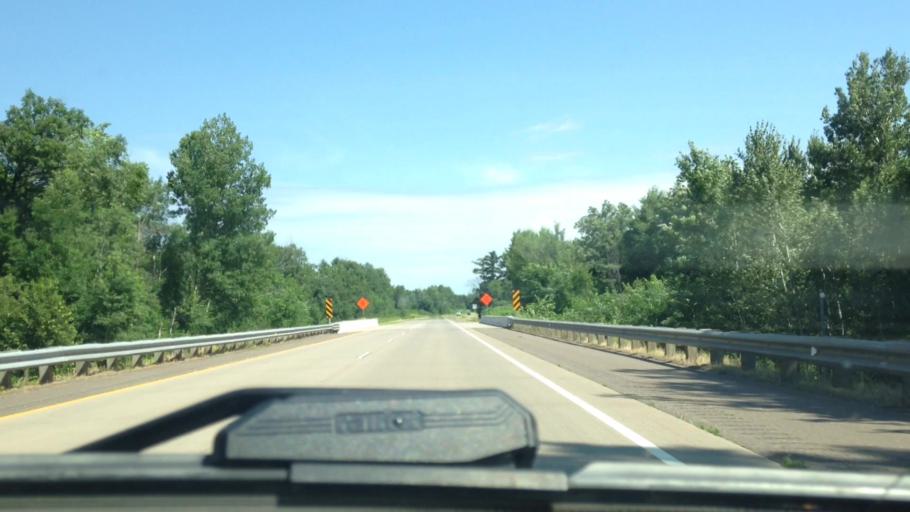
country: US
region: Wisconsin
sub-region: Barron County
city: Rice Lake
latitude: 45.5530
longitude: -91.7645
